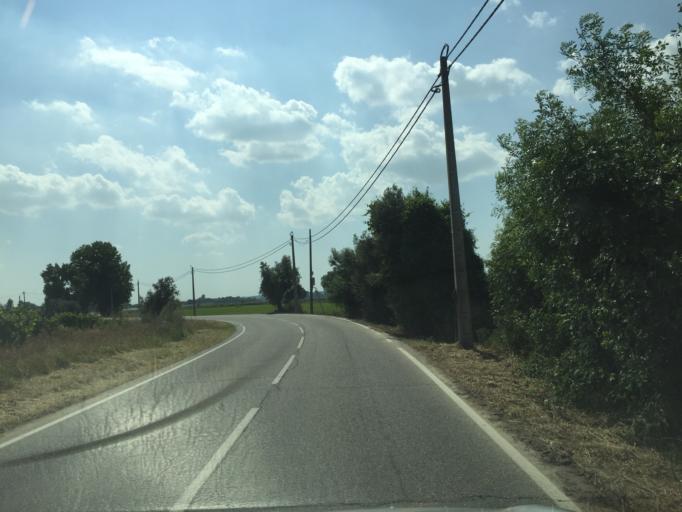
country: PT
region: Santarem
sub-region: Alpiarca
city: Alpiarca
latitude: 39.3028
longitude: -8.5457
